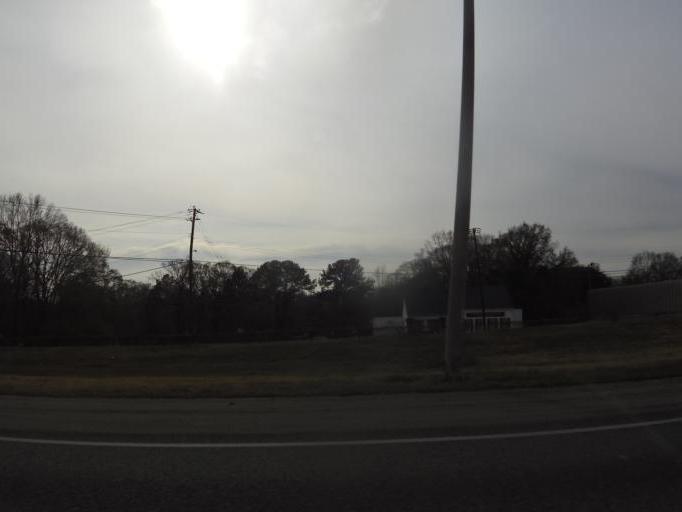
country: US
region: Alabama
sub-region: Montgomery County
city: Montgomery
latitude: 32.3657
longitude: -86.2760
